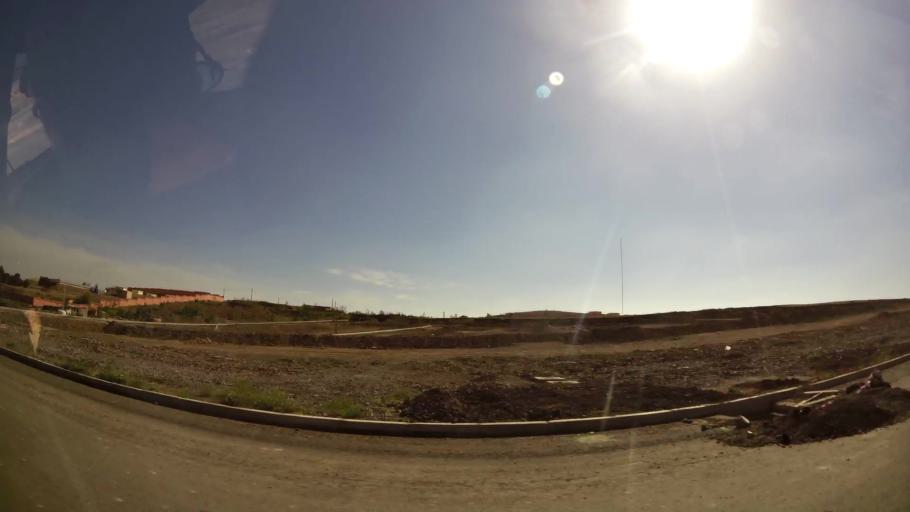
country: MA
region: Oriental
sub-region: Oujda-Angad
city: Oujda
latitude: 34.6489
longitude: -1.9526
